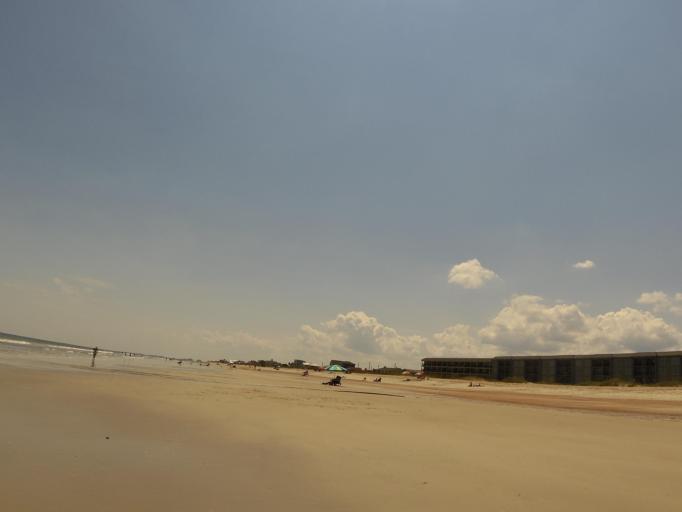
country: US
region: Florida
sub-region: Nassau County
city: Fernandina Beach
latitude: 30.6628
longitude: -81.4304
